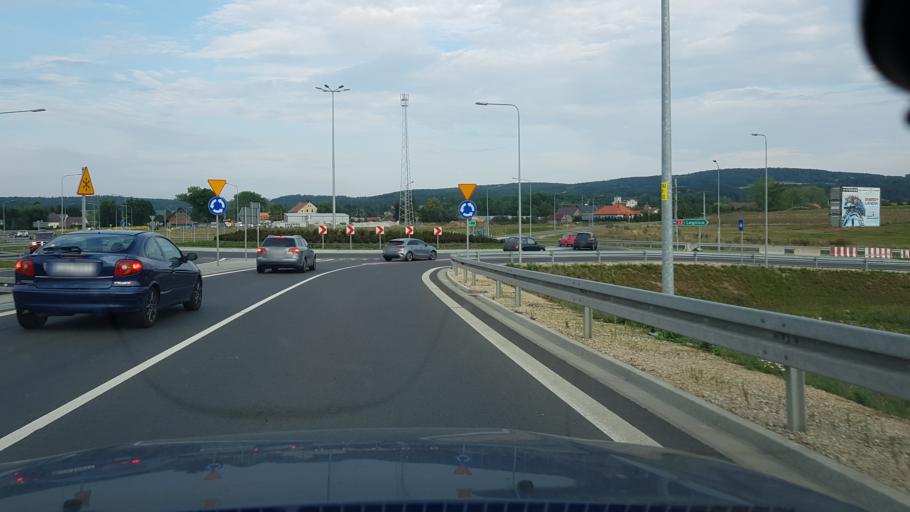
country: PL
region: Lower Silesian Voivodeship
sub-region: Powiat jaworski
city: Bolkow
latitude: 50.9112
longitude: 16.1566
